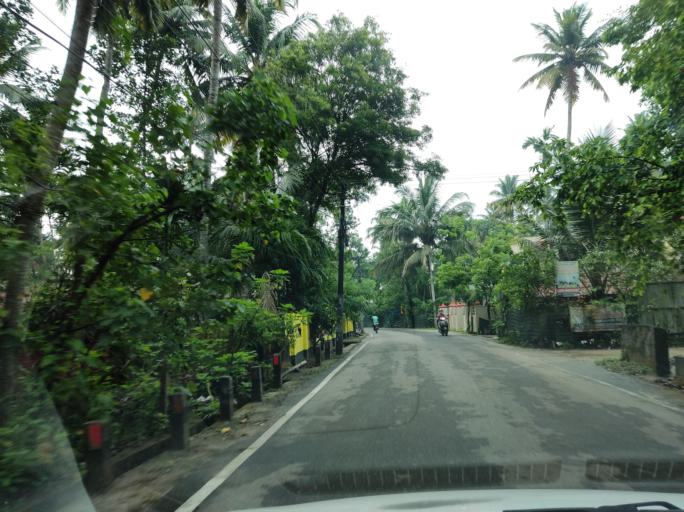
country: IN
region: Kerala
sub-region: Alappuzha
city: Kayankulam
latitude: 9.1940
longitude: 76.4674
